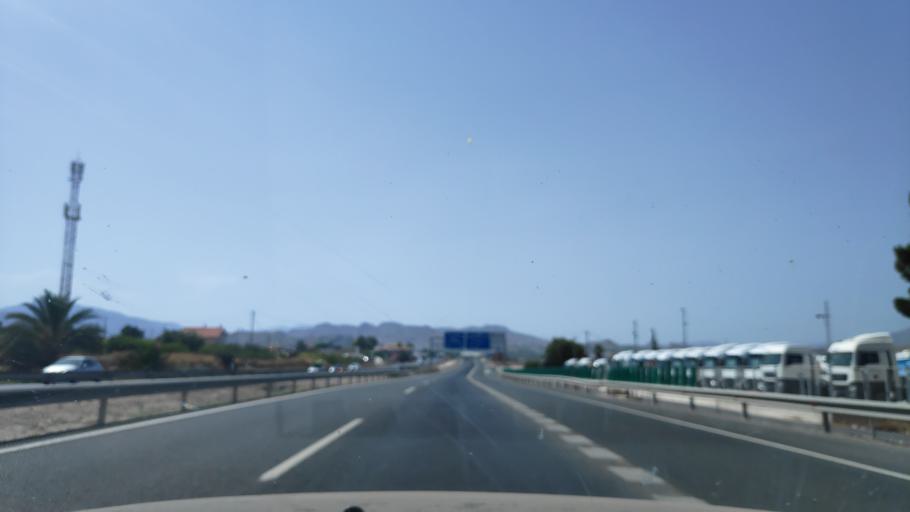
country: ES
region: Murcia
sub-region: Murcia
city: Lorqui
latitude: 38.1213
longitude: -1.2494
